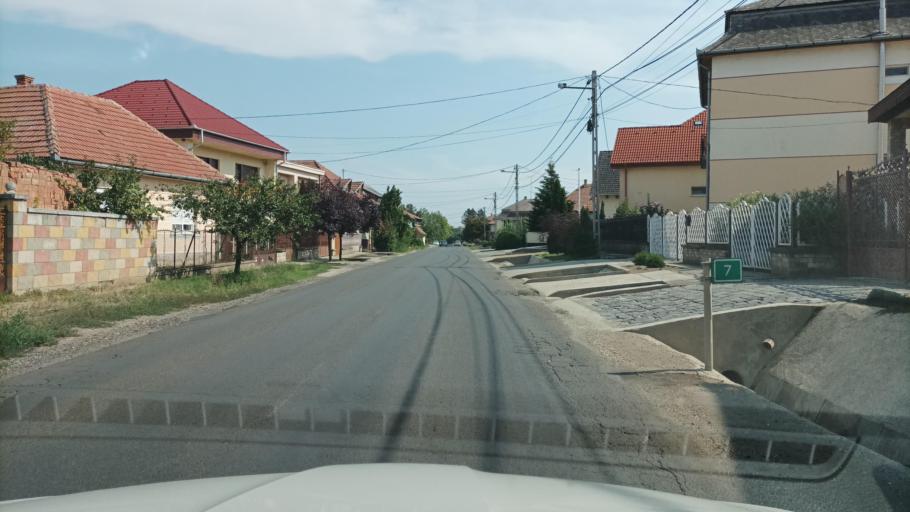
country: HU
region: Pest
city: Galgaheviz
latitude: 47.6226
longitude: 19.5436
